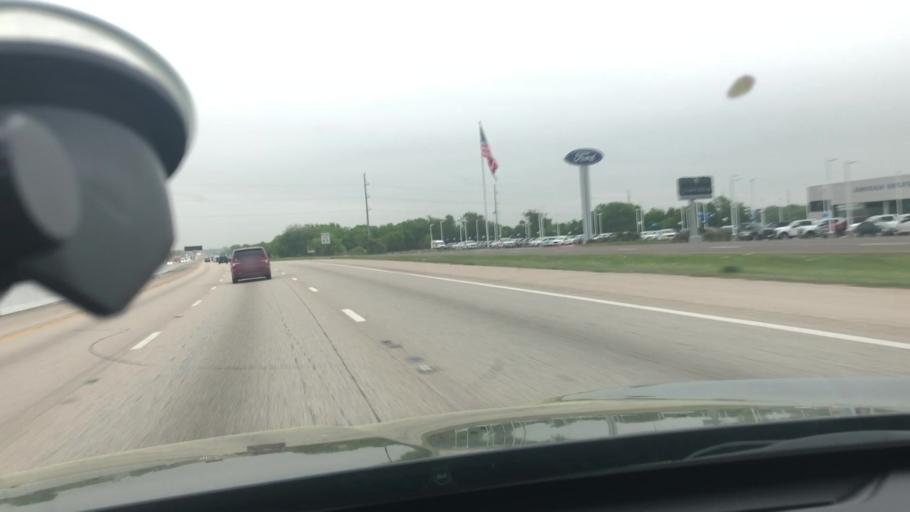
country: US
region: Texas
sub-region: Bell County
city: Belton
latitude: 31.0615
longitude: -97.4347
